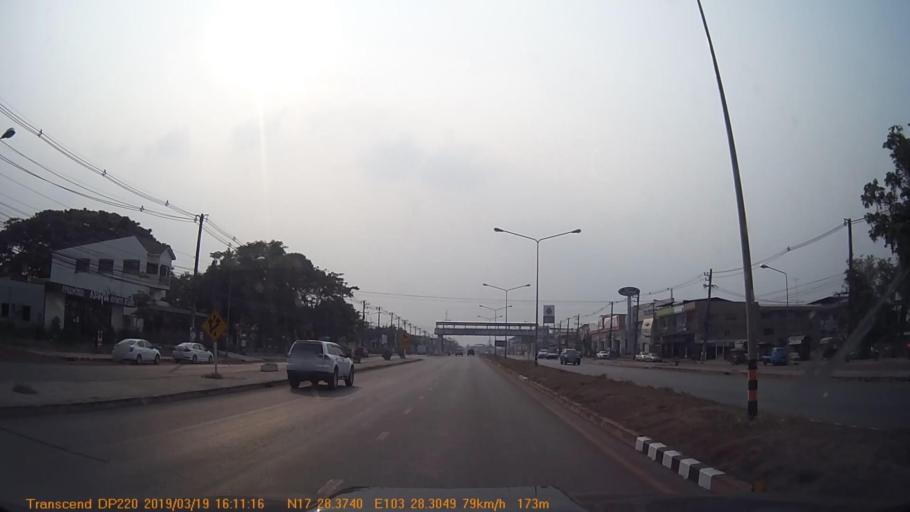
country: TH
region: Sakon Nakhon
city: Sawang Daen Din
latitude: 17.4730
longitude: 103.4712
